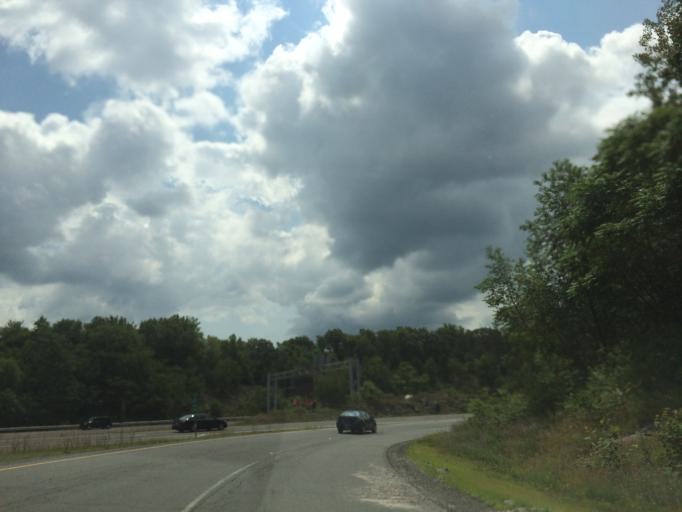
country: US
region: Pennsylvania
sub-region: Luzerne County
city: Hudson
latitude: 41.2486
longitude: -75.8217
